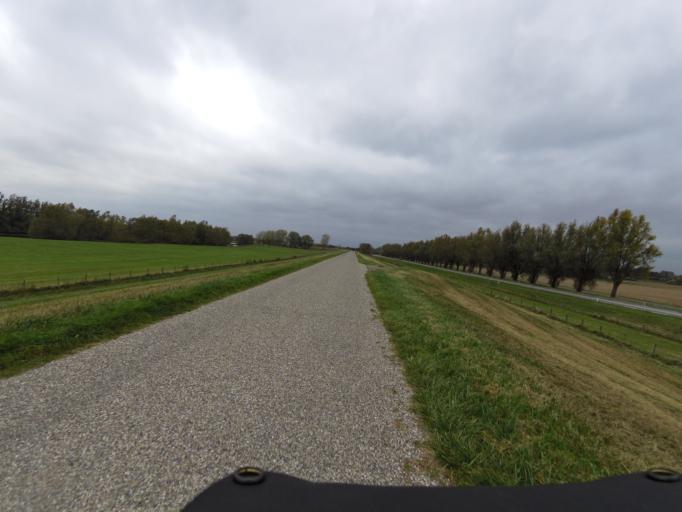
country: NL
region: Gelderland
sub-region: Gemeente Zevenaar
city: Zevenaar
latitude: 51.8765
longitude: 6.1005
